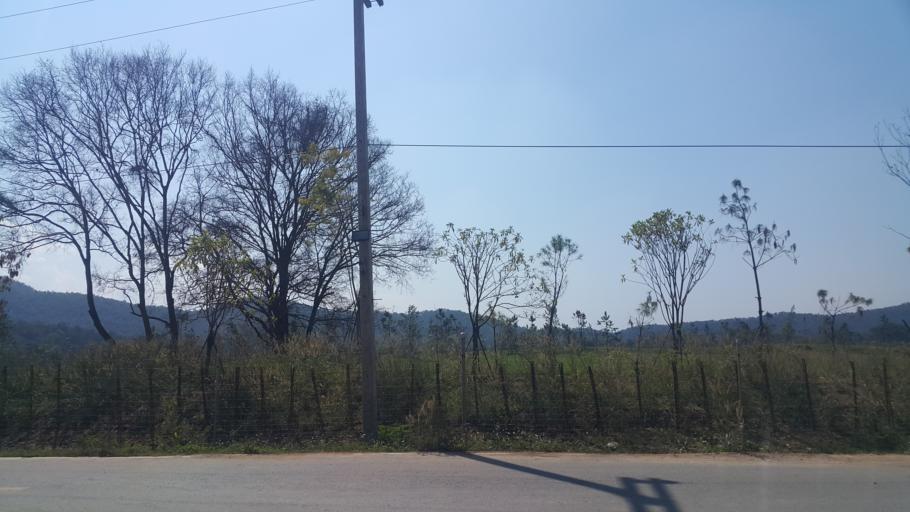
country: TH
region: Lamphun
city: Ban Thi
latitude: 18.6852
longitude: 99.1683
